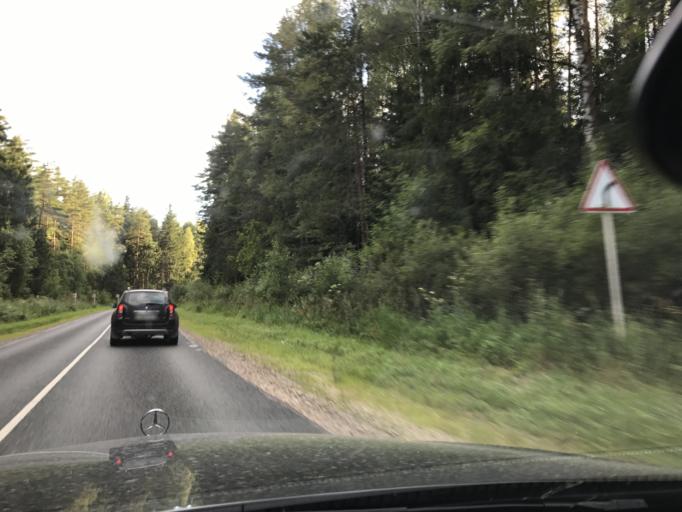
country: RU
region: Vladimir
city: Raduzhnyy
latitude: 55.9857
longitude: 40.2575
